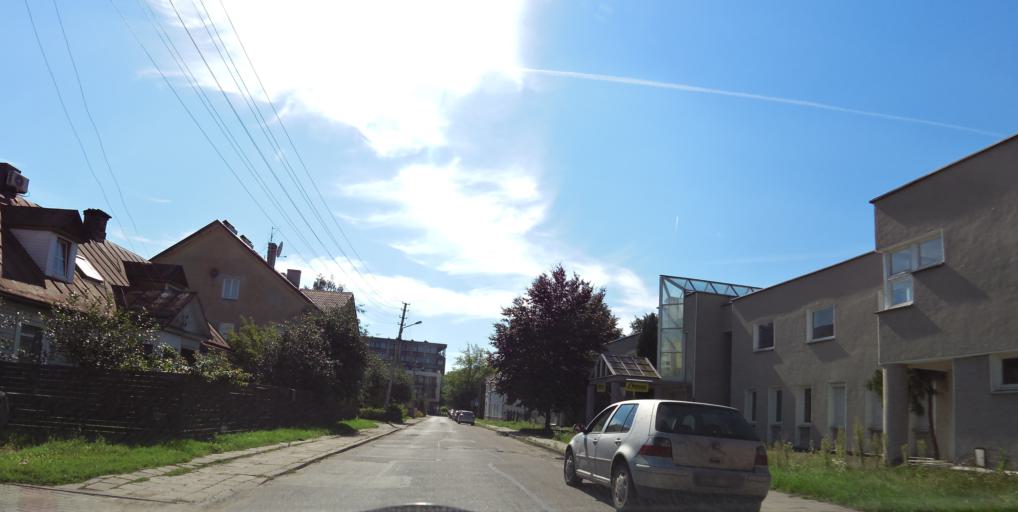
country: LT
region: Vilnius County
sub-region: Vilnius
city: Vilnius
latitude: 54.6948
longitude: 25.2946
